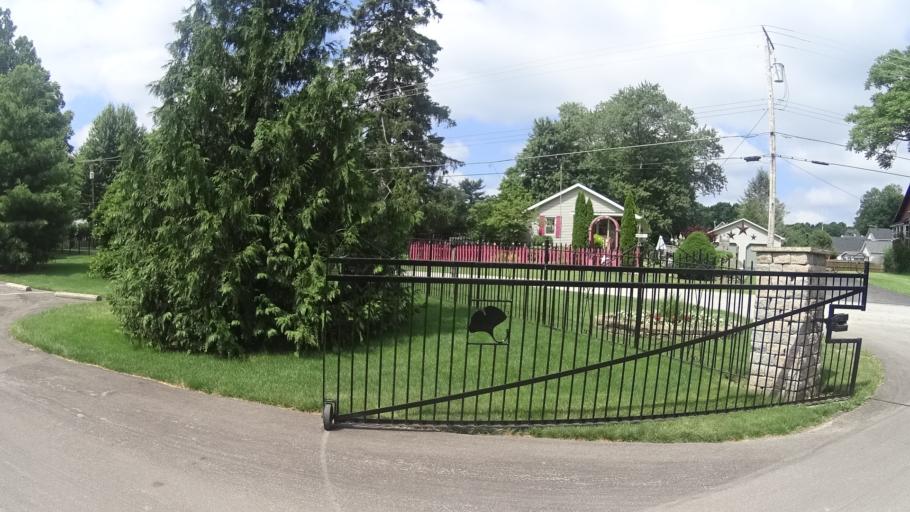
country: US
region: Ohio
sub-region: Huron County
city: Wakeman
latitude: 41.3310
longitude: -82.3507
